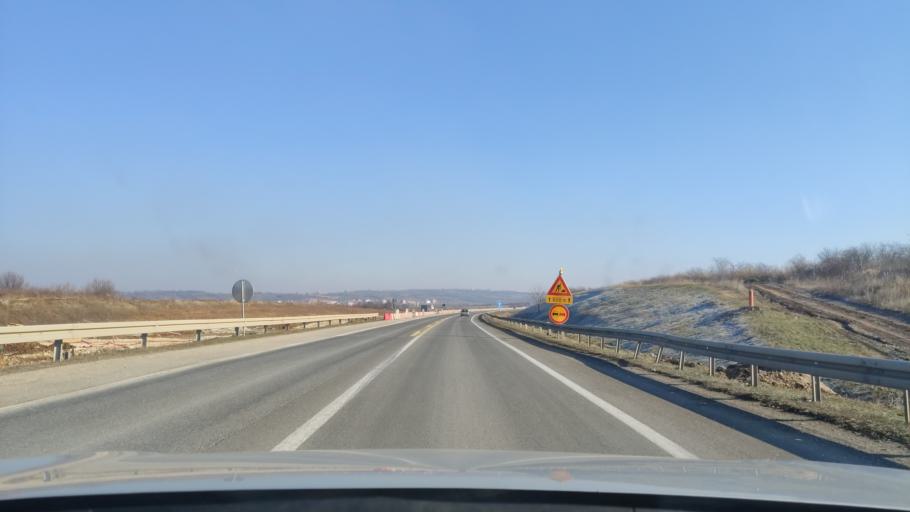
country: RS
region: Central Serbia
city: Sremcica
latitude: 44.7130
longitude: 20.3850
